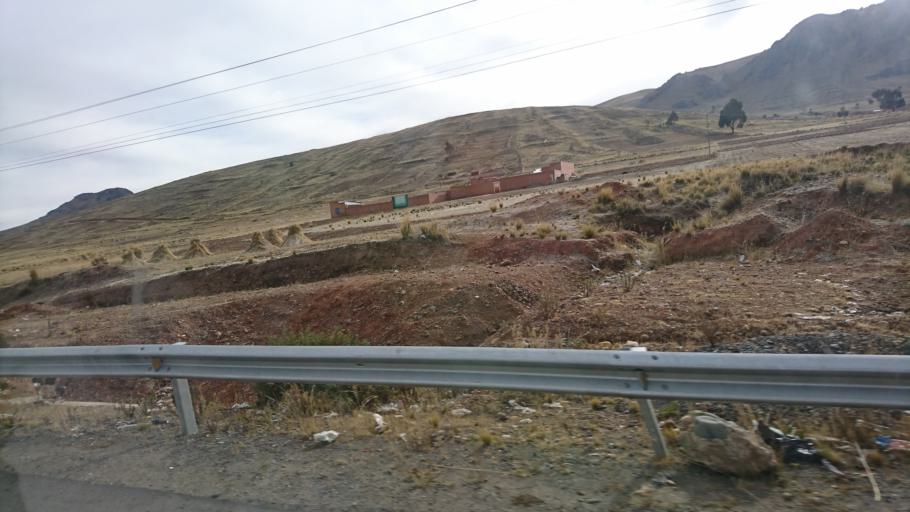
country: BO
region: La Paz
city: La Paz
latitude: -16.4122
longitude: -68.3475
